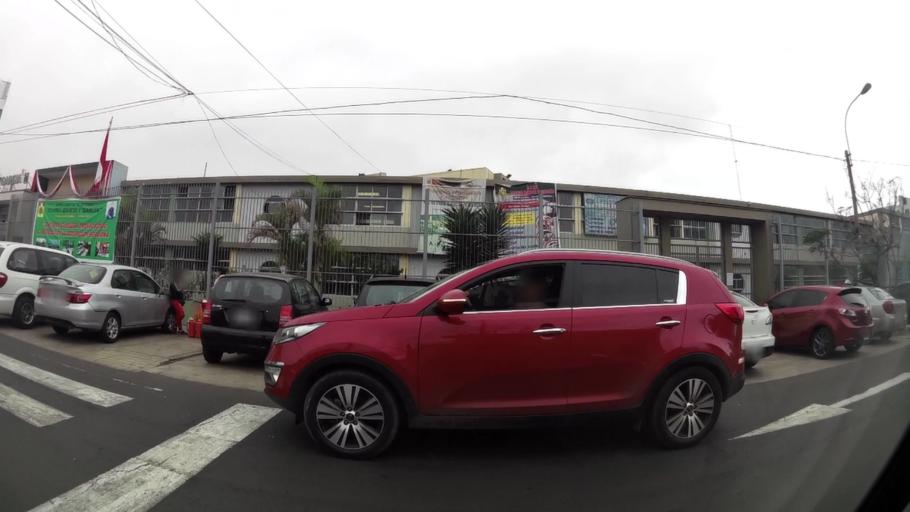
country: PE
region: Lima
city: Lima
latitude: -12.0679
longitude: -77.0547
